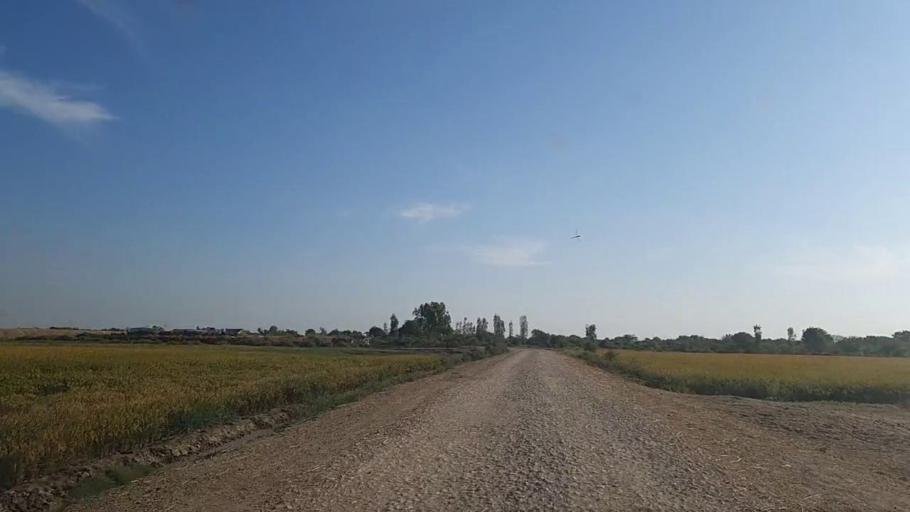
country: PK
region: Sindh
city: Mirpur Batoro
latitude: 24.7536
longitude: 68.3678
